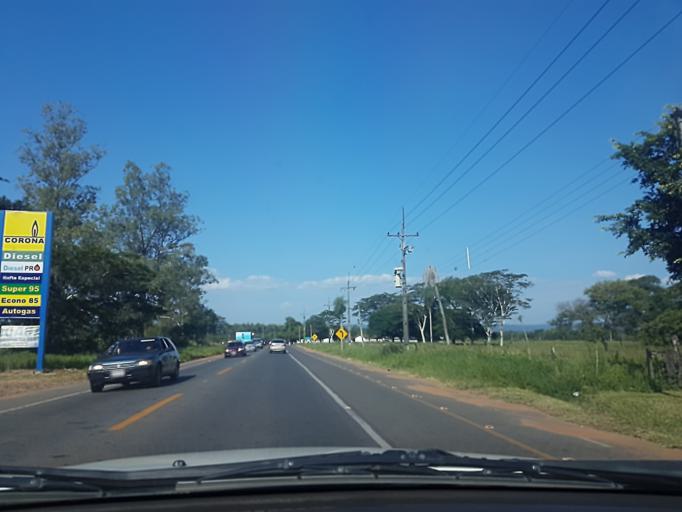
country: PY
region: Central
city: Aregua
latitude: -25.2386
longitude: -57.4243
